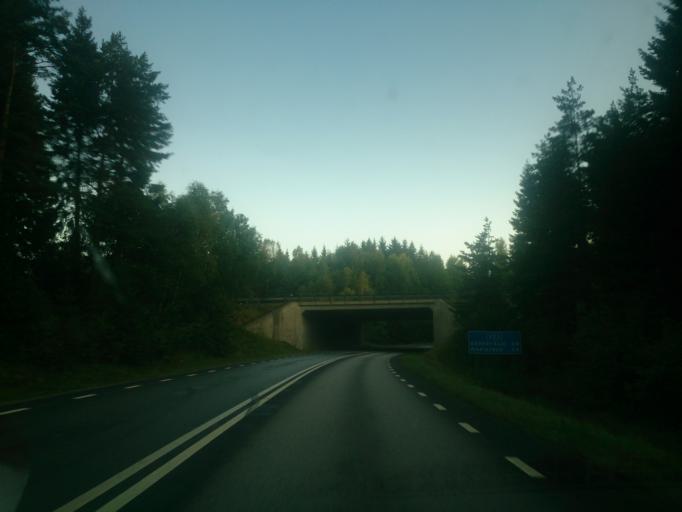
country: SE
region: Soedermanland
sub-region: Nykopings Kommun
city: Nykoping
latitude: 58.7854
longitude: 17.0716
